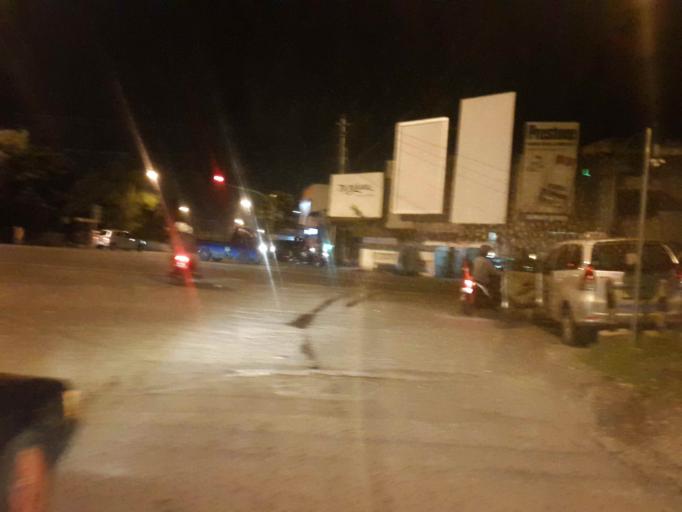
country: ID
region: Central Java
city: Surakarta
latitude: -7.5525
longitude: 110.8213
